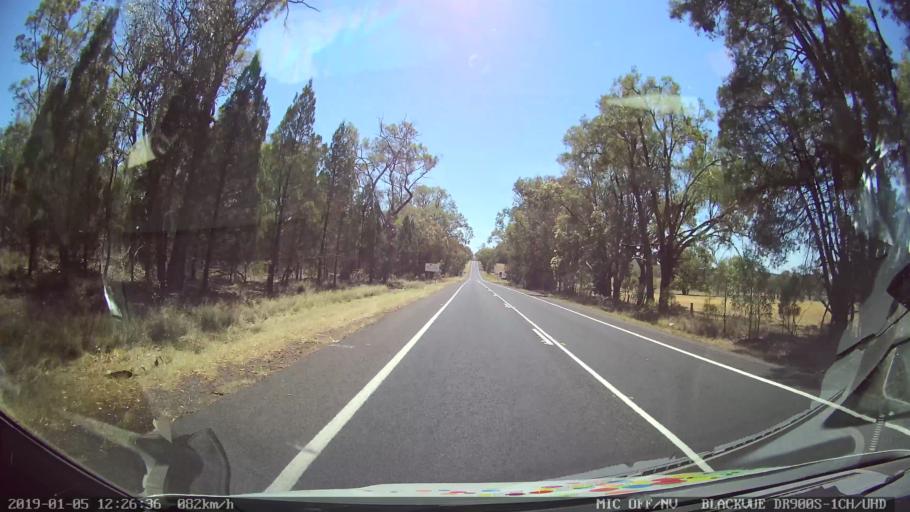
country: AU
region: New South Wales
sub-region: Warrumbungle Shire
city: Coonabarabran
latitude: -31.2534
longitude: 149.2976
